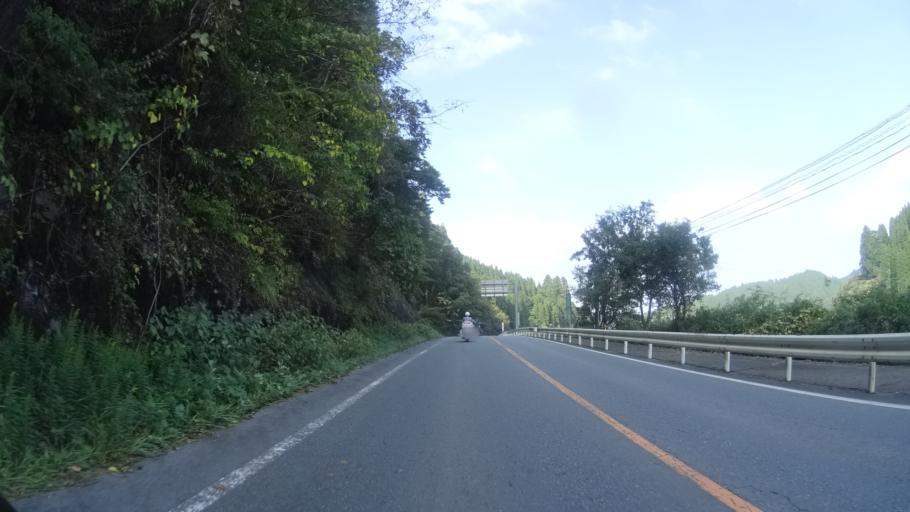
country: JP
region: Kumamoto
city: Aso
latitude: 33.0931
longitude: 131.0662
